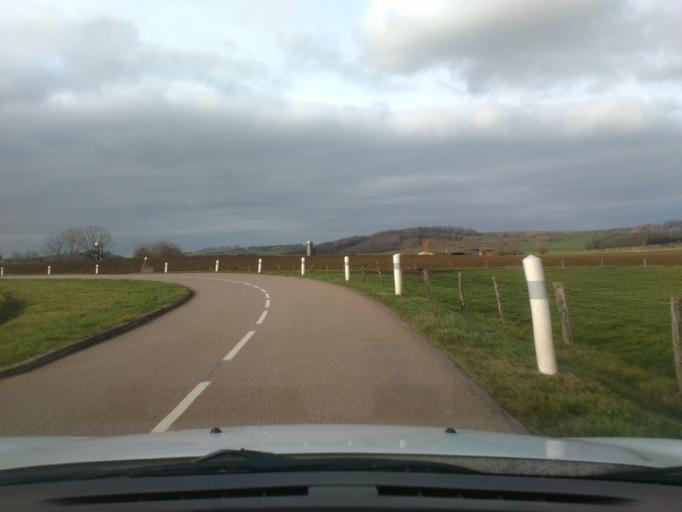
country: FR
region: Lorraine
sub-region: Departement des Vosges
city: Mirecourt
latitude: 48.3322
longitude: 6.0303
